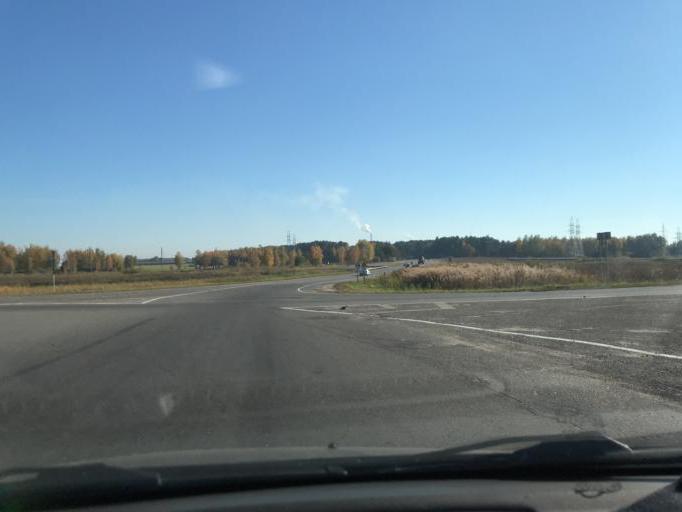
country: BY
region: Gomel
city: Kastsyukowka
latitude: 52.4523
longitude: 30.8249
